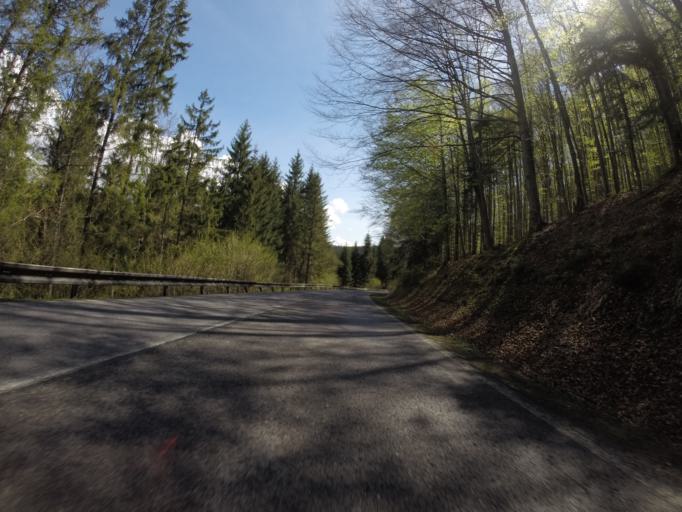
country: SK
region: Banskobystricky
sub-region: Okres Banska Bystrica
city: Brezno
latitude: 48.8435
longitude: 19.6489
